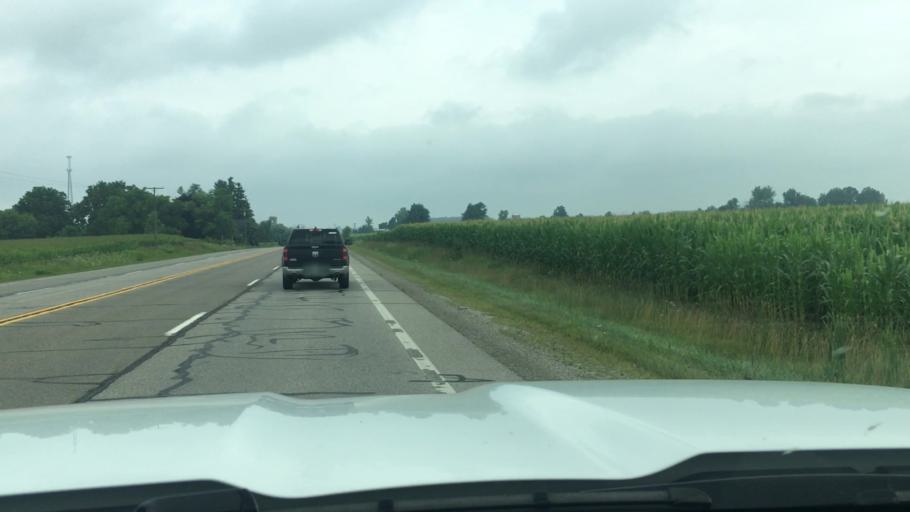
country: US
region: Michigan
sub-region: Sanilac County
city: Brown City
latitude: 43.2179
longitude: -83.0775
